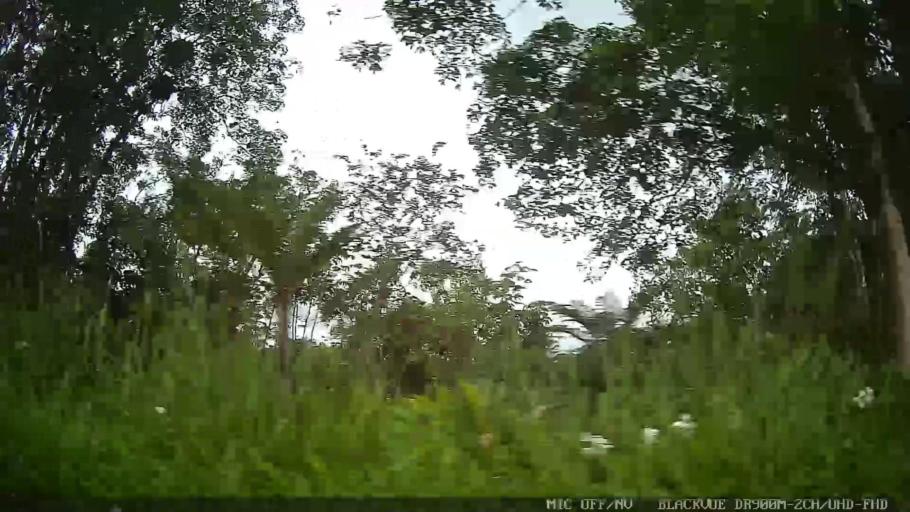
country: BR
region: Sao Paulo
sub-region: Itanhaem
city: Itanhaem
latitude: -24.0993
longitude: -46.8023
